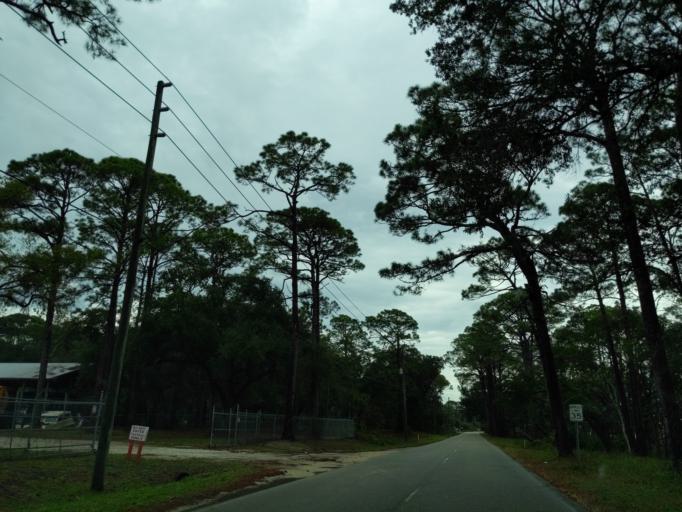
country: US
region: Florida
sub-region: Franklin County
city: Eastpoint
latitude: 29.7335
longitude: -84.8842
